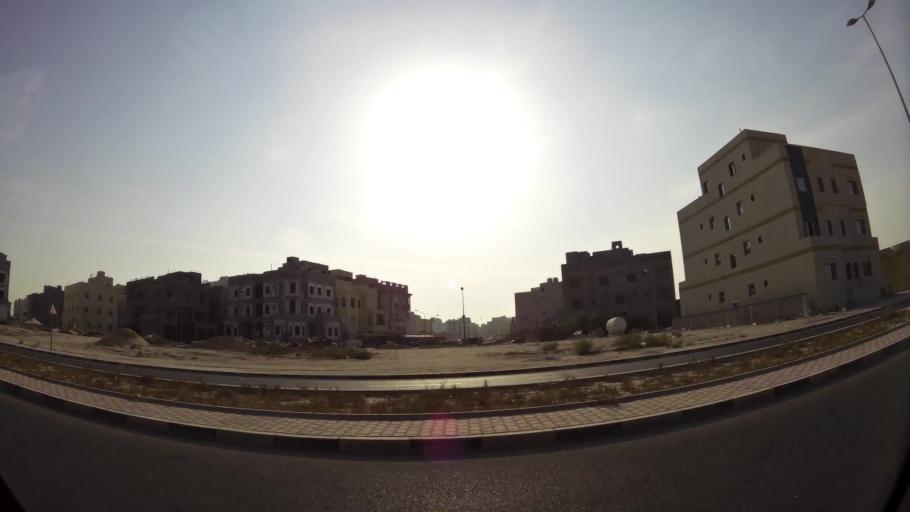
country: KW
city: Al Funaytis
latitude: 29.2063
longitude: 48.1001
